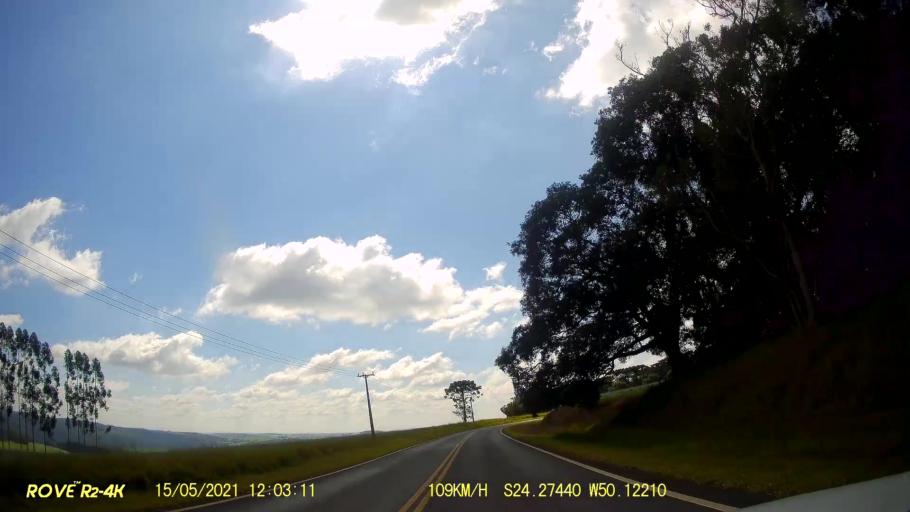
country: BR
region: Parana
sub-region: Pirai Do Sul
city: Pirai do Sul
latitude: -24.2744
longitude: -50.1223
